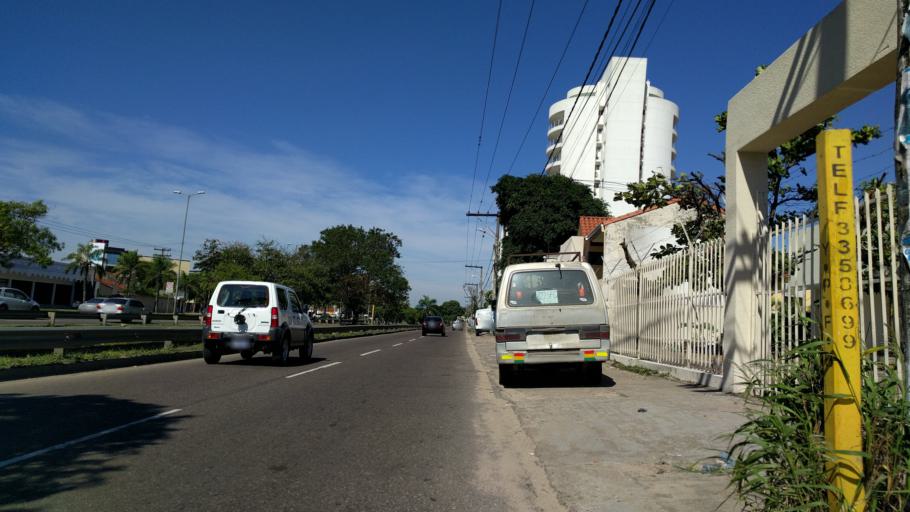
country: BO
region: Santa Cruz
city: Santa Cruz de la Sierra
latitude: -17.7909
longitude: -63.1947
